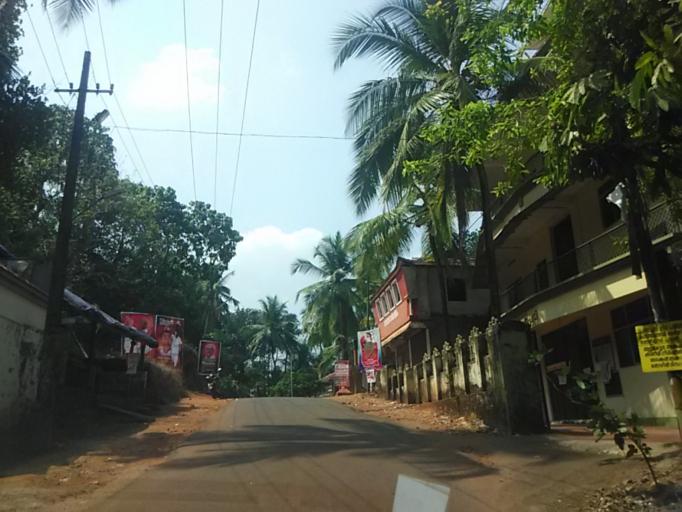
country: IN
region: Kerala
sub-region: Kozhikode
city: Naduvannur
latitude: 11.5264
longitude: 75.7586
